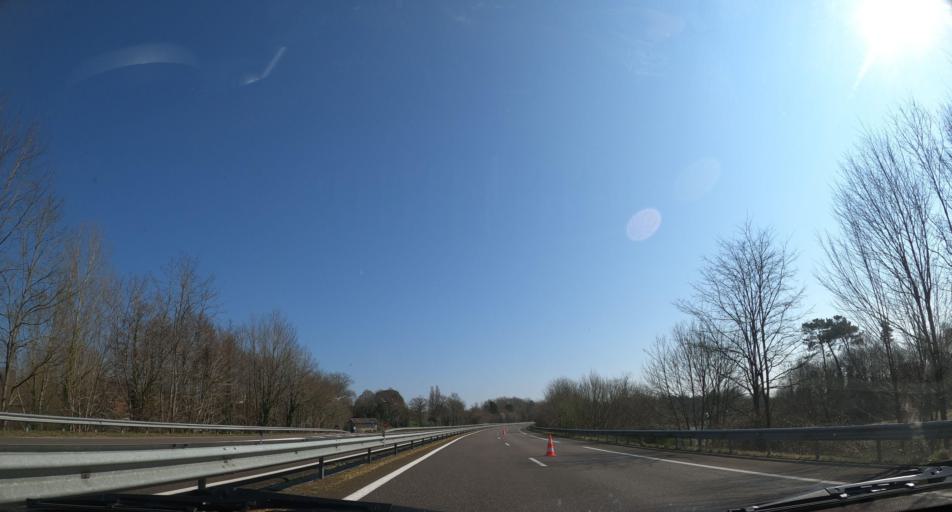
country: FR
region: Aquitaine
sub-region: Departement des Landes
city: Meilhan
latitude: 43.8617
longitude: -0.7105
